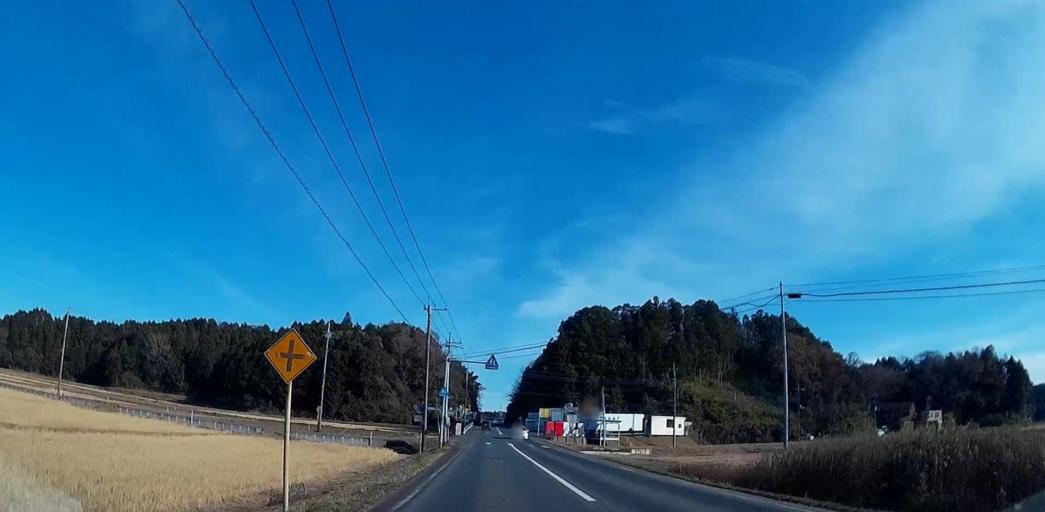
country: JP
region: Chiba
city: Yokaichiba
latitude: 35.7349
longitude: 140.5374
